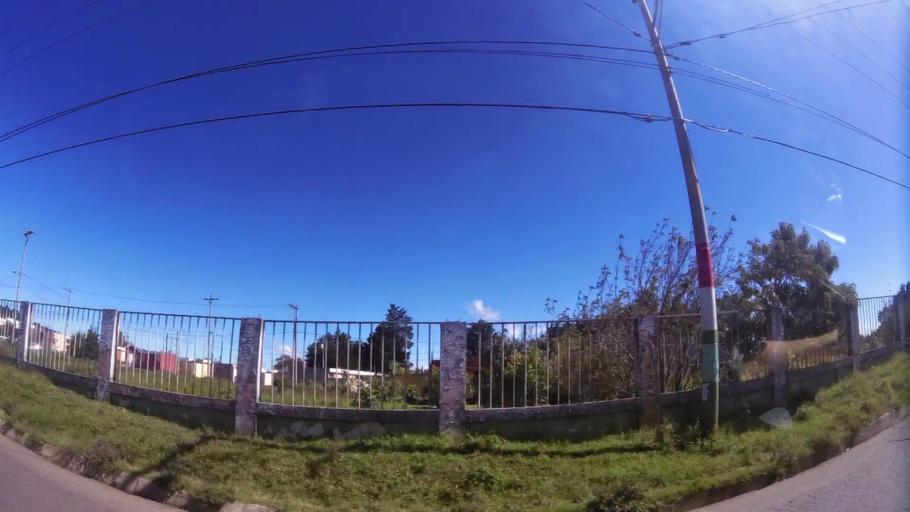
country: GT
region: Guatemala
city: San Jose Pinula
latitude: 14.5112
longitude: -90.4247
